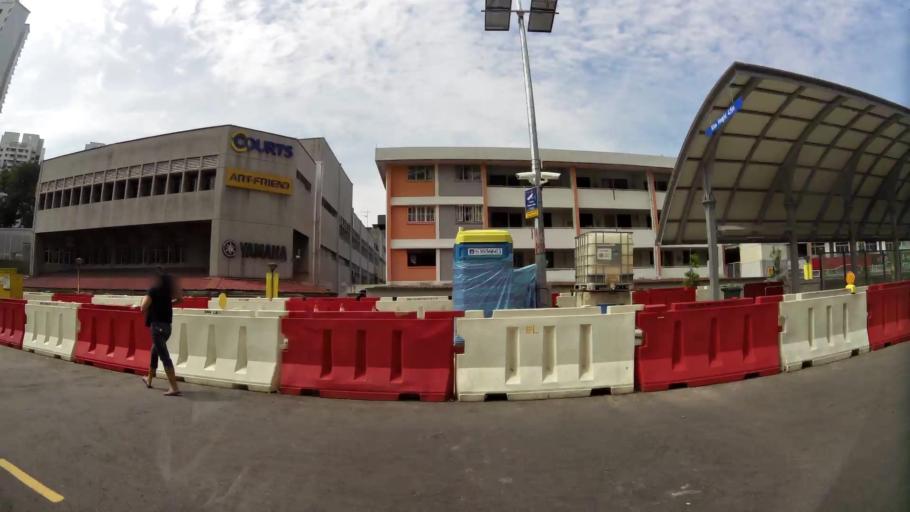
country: SG
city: Singapore
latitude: 1.3136
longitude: 103.7657
